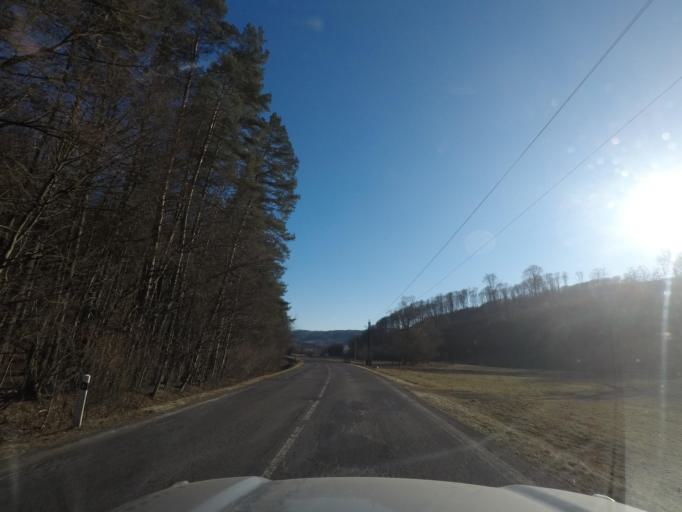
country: SK
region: Presovsky
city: Medzilaborce
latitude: 49.2711
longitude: 21.8000
